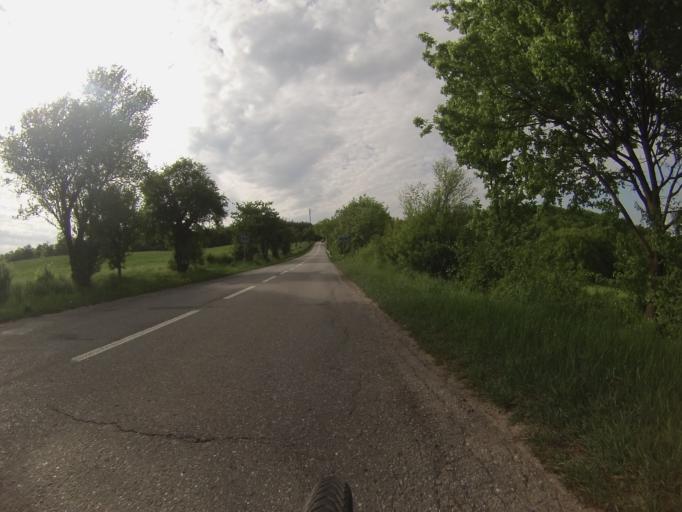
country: CZ
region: South Moravian
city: Veverska Bityska
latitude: 49.2550
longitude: 16.4515
